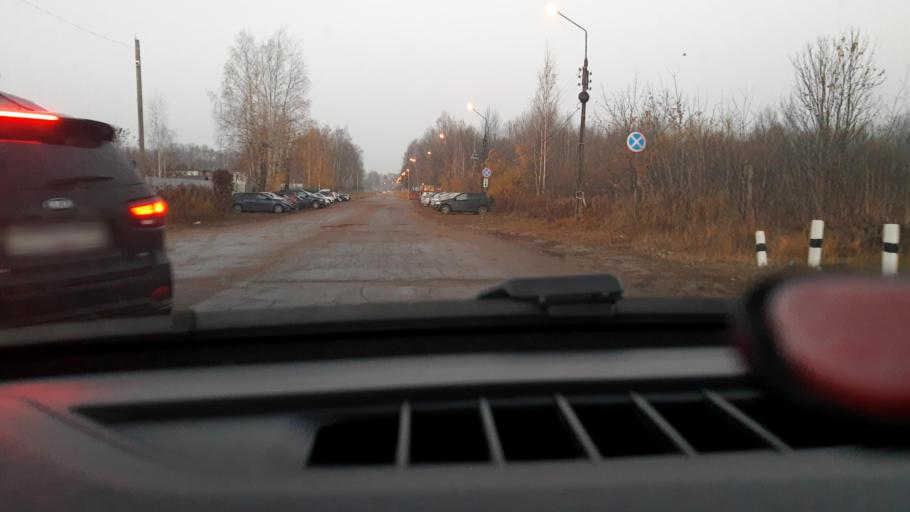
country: RU
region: Nizjnij Novgorod
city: Gorbatovka
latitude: 56.3254
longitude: 43.8379
